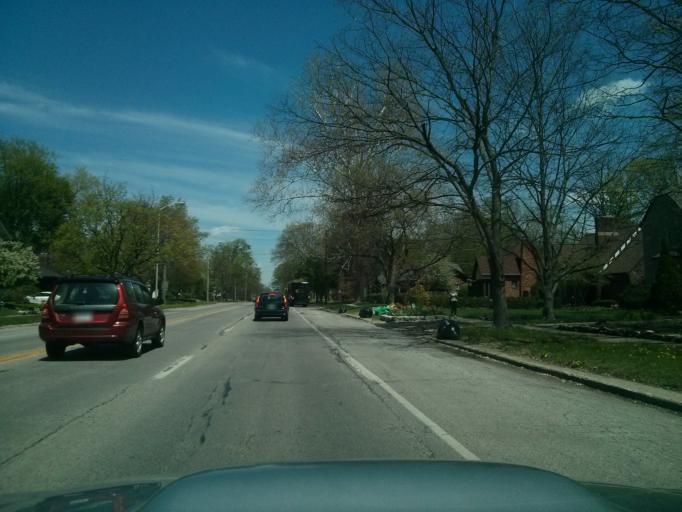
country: US
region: Indiana
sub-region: Marion County
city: Broad Ripple
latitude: 39.8581
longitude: -86.1458
